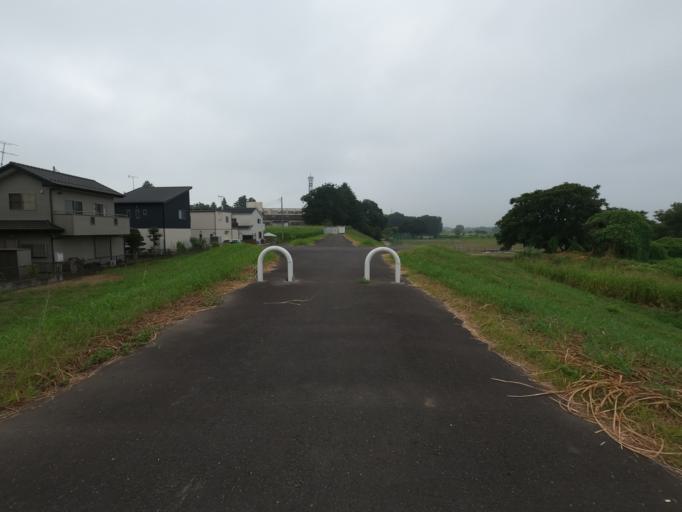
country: JP
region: Ibaraki
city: Mitsukaido
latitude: 36.0187
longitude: 139.9828
